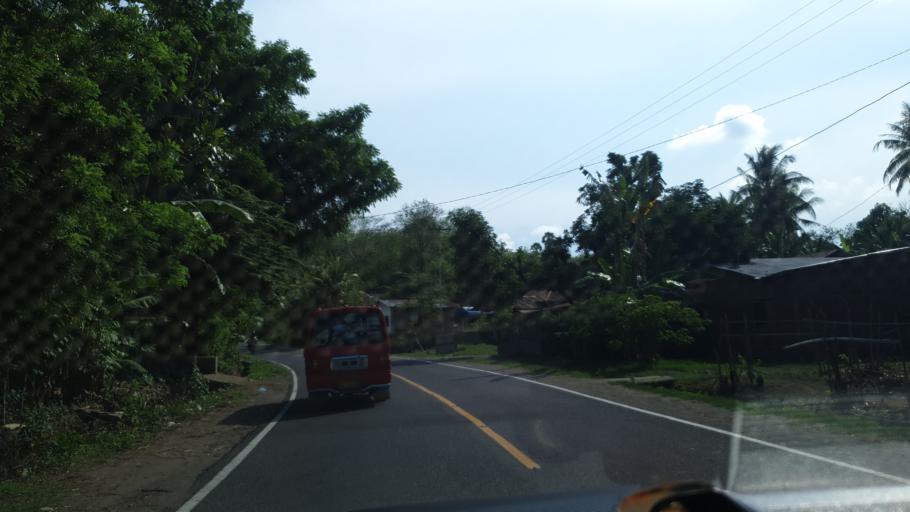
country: ID
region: East Nusa Tenggara
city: Nangalimang
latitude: -8.6420
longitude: 122.2062
